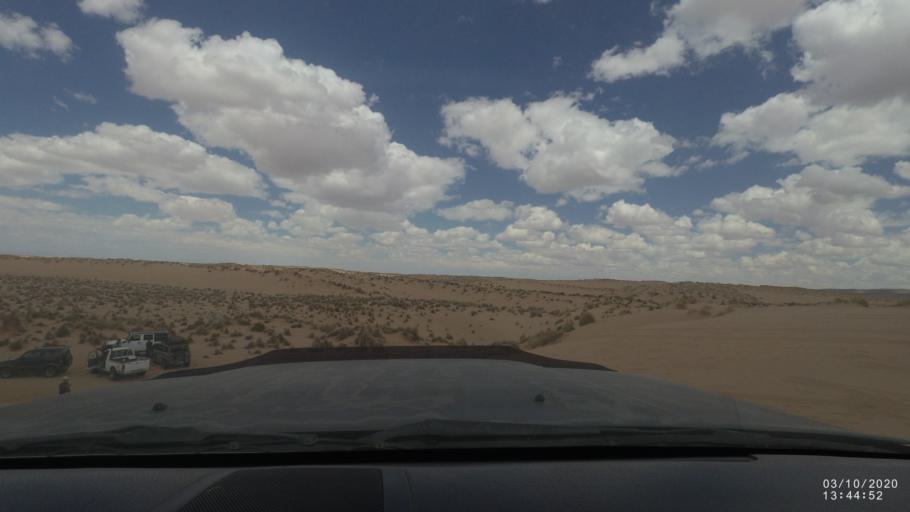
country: BO
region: Oruro
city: Poopo
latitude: -18.6918
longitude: -67.5294
